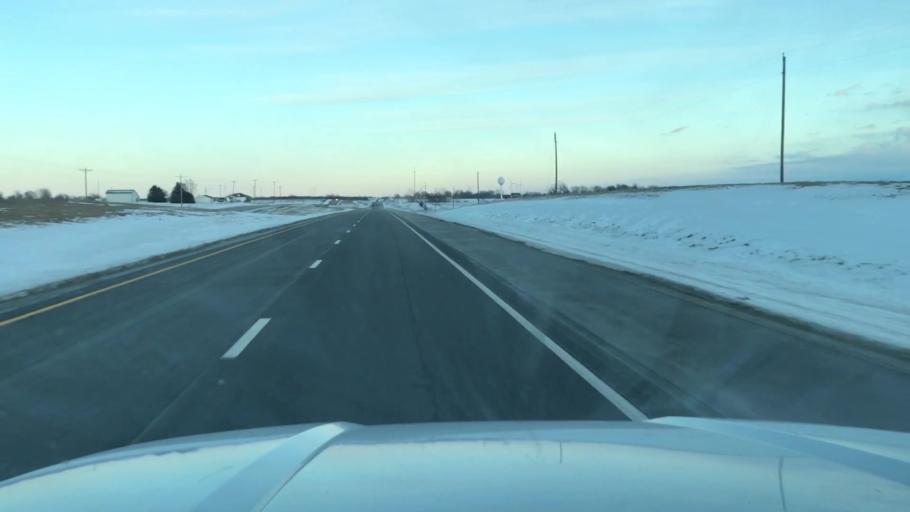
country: US
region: Missouri
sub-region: Clinton County
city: Gower
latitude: 39.7620
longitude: -94.5223
